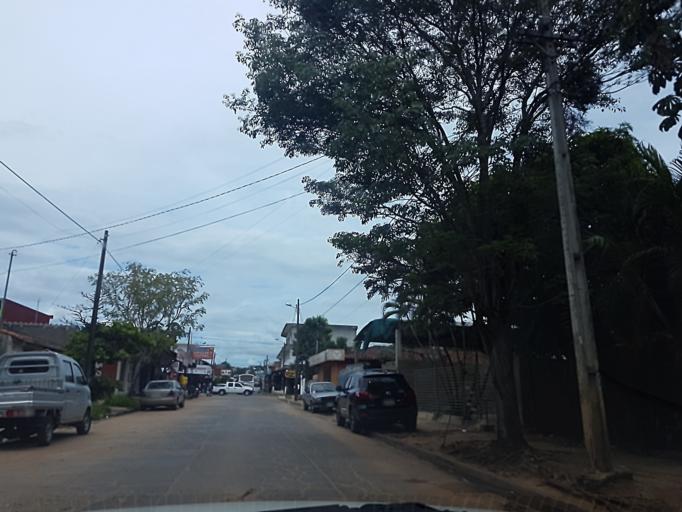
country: PY
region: Central
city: Limpio
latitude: -25.1703
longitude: -57.4765
